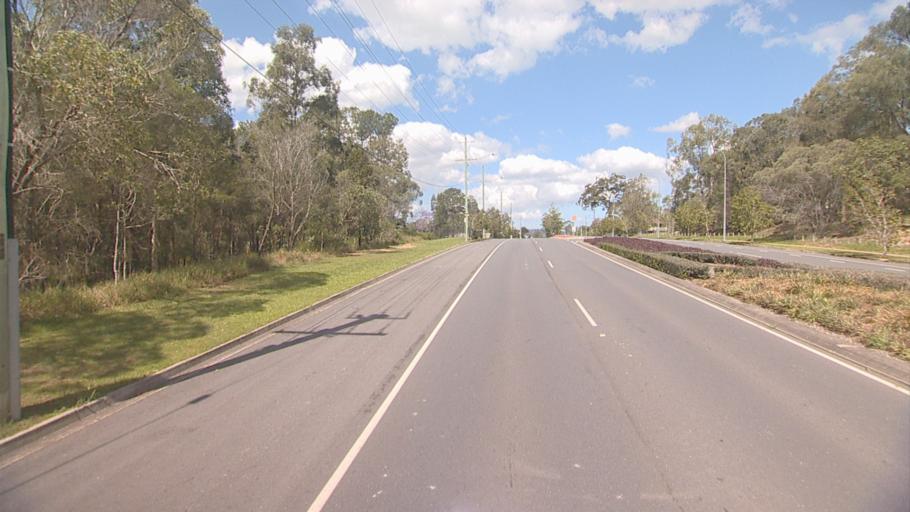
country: AU
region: Queensland
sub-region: Logan
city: Woodridge
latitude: -27.6174
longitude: 153.0959
